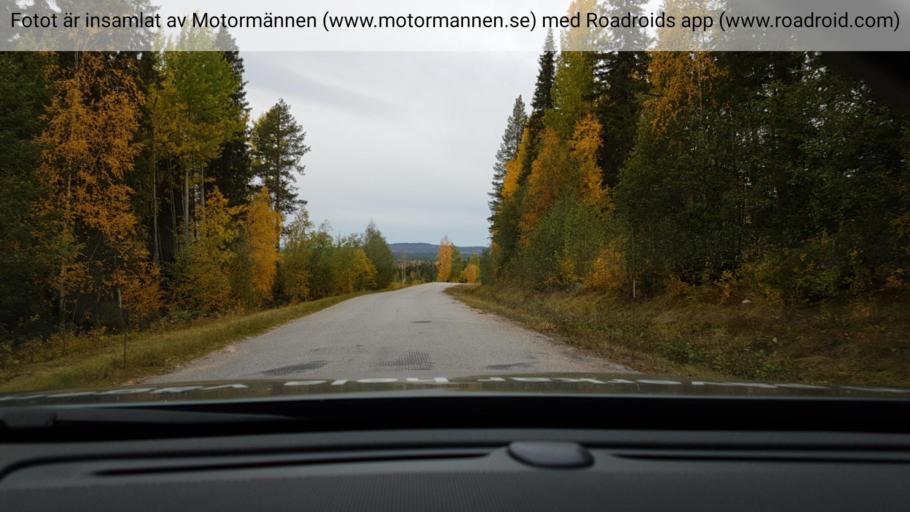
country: SE
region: Norrbotten
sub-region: Overkalix Kommun
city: OEverkalix
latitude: 66.2351
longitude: 22.9832
